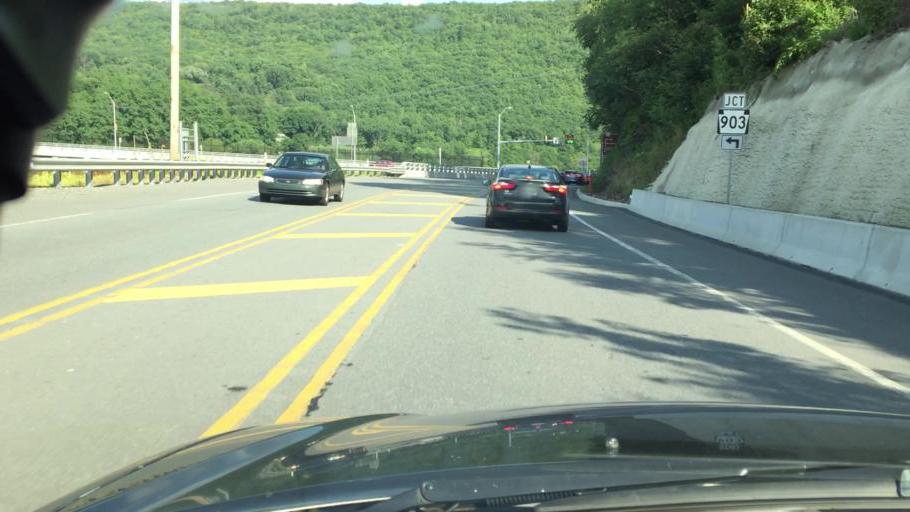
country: US
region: Pennsylvania
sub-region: Carbon County
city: Jim Thorpe
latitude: 40.8696
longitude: -75.7401
